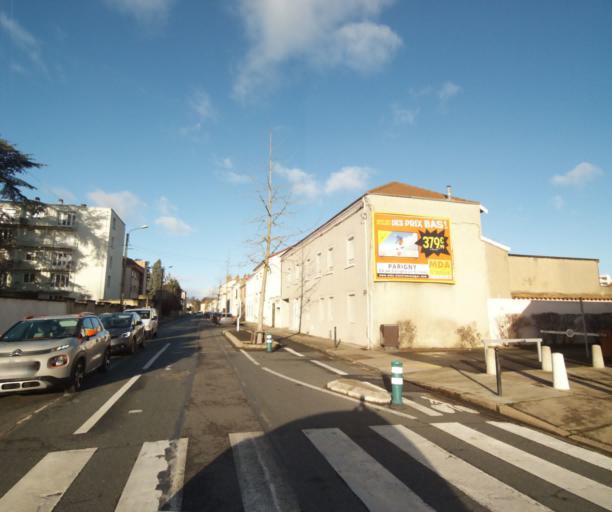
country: FR
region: Rhone-Alpes
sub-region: Departement de la Loire
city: Roanne
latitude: 46.0448
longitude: 4.0797
